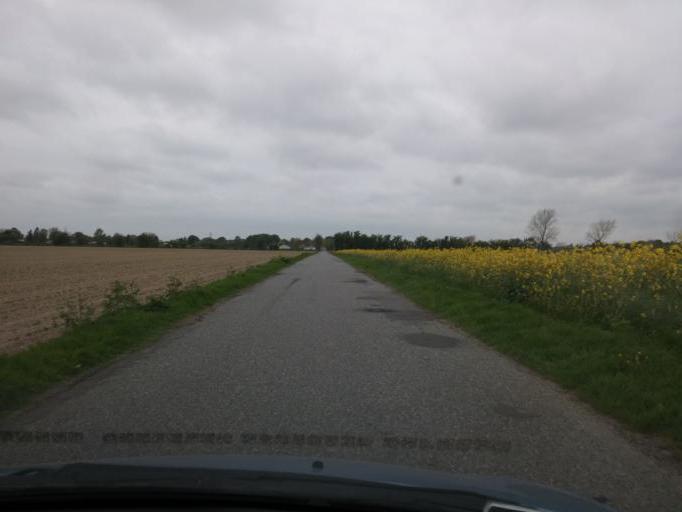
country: DK
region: South Denmark
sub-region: Odense Kommune
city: Bullerup
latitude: 55.4065
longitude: 10.5239
